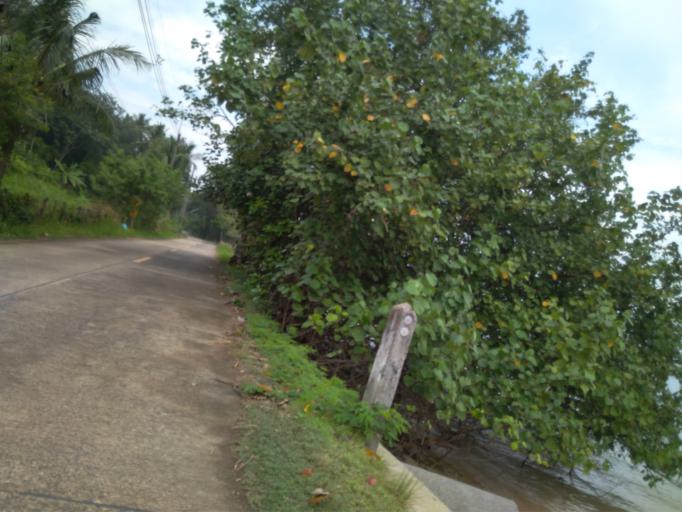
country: TH
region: Phangnga
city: Ko Yao
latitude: 8.1116
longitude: 98.6231
